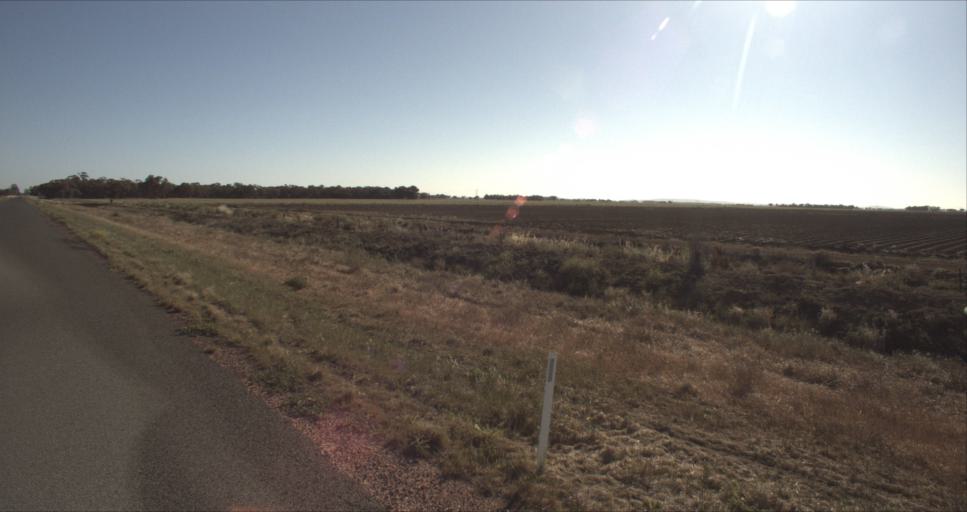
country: AU
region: New South Wales
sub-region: Leeton
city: Leeton
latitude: -34.5682
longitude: 146.2640
